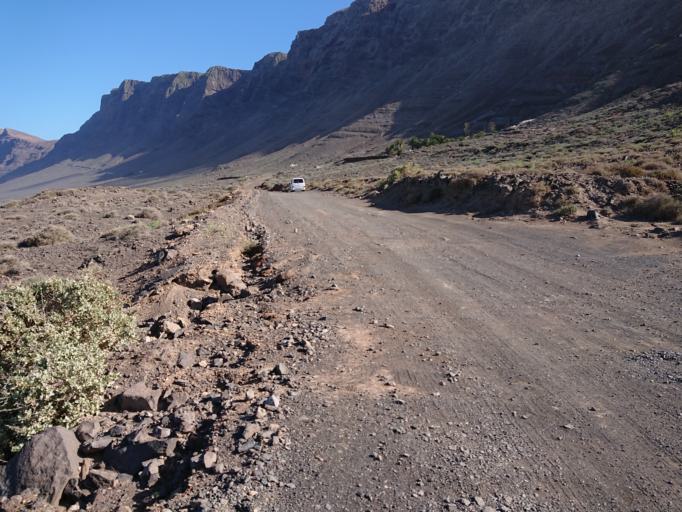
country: ES
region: Canary Islands
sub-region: Provincia de Las Palmas
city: Haria
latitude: 29.1168
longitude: -13.5407
